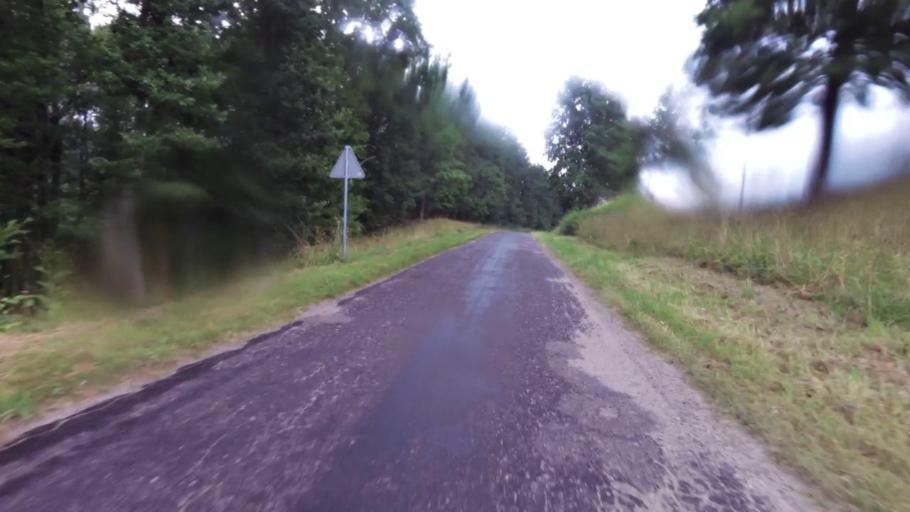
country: PL
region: West Pomeranian Voivodeship
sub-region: Powiat lobeski
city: Wegorzyno
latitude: 53.5186
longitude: 15.6473
